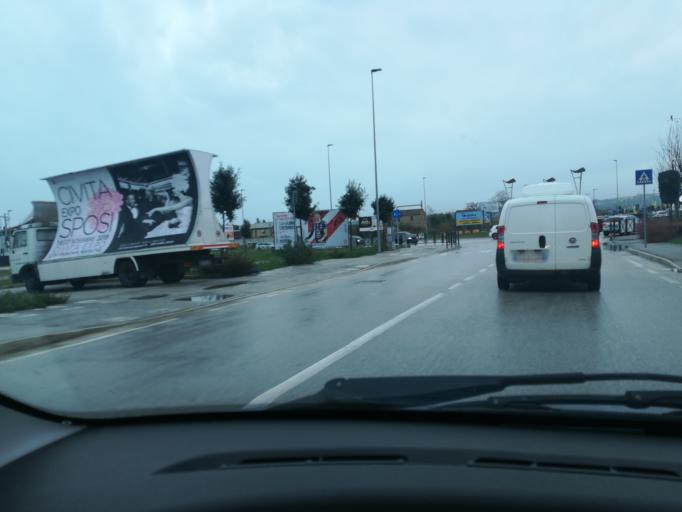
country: IT
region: The Marches
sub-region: Provincia di Macerata
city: Santa Maria Apparente
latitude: 43.2948
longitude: 13.7023
